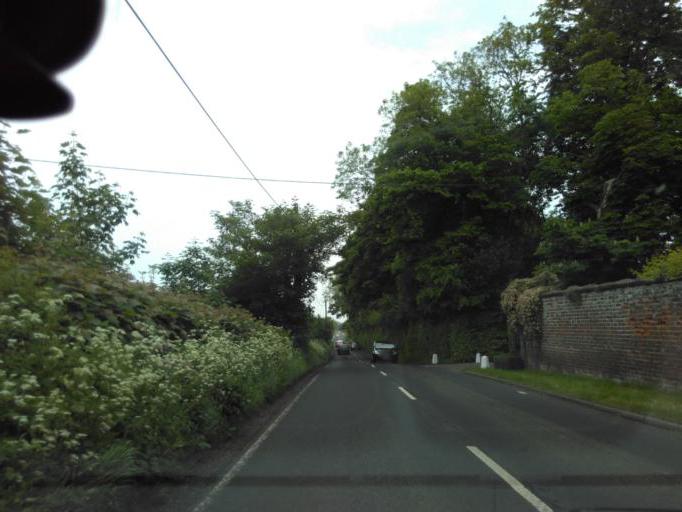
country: GB
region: England
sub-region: Kent
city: Lyminge
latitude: 51.1677
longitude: 1.0524
